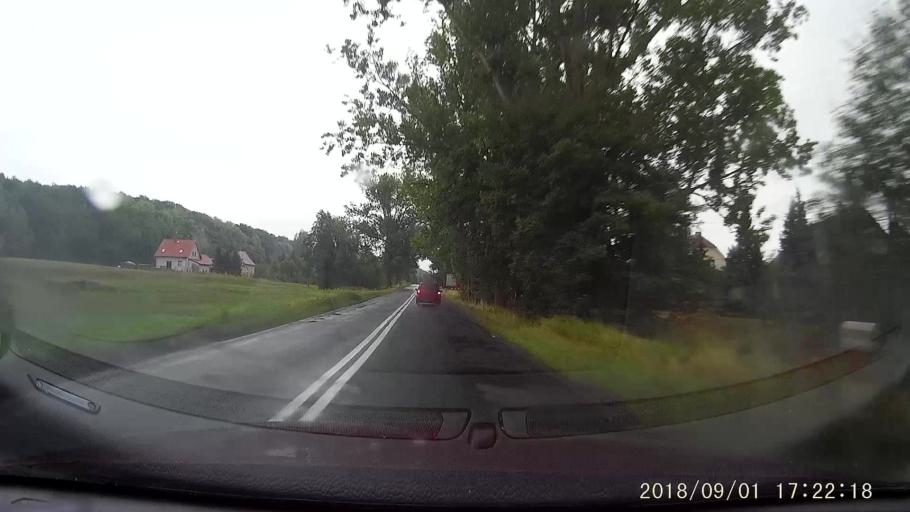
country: PL
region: Lubusz
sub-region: Powiat zaganski
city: Zagan
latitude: 51.7067
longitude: 15.2893
